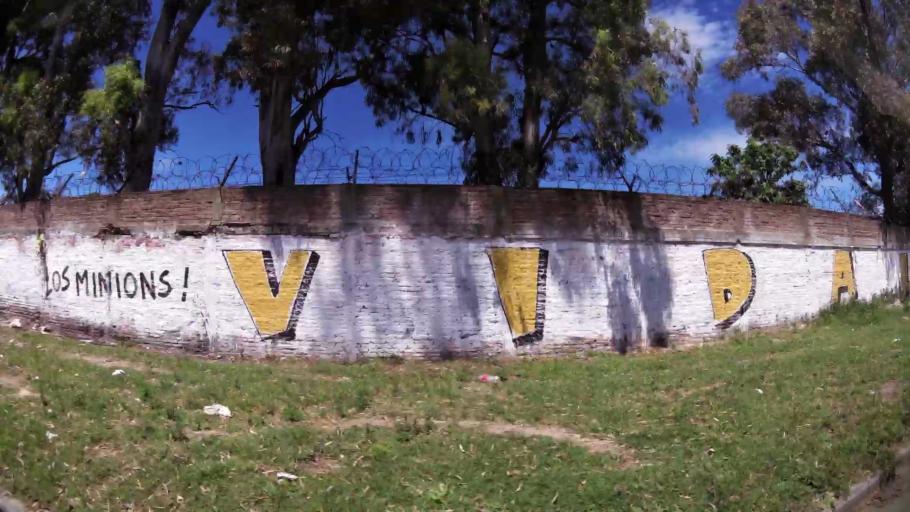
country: AR
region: Buenos Aires
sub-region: Partido de Quilmes
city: Quilmes
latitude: -34.7301
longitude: -58.3210
